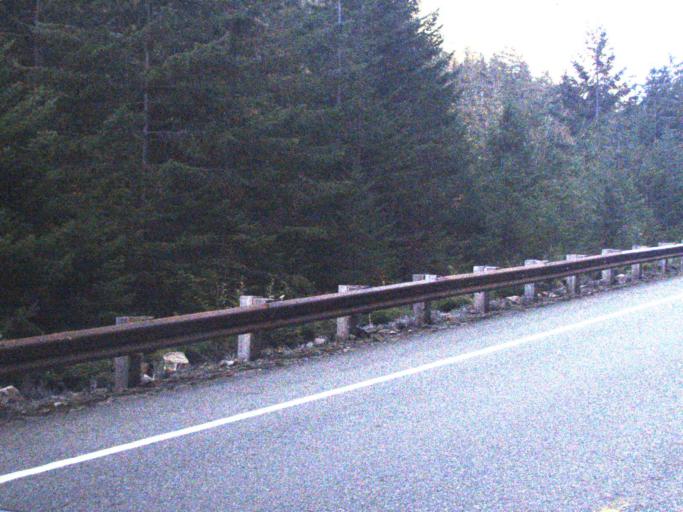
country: US
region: Washington
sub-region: Snohomish County
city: Darrington
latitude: 48.6757
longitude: -120.8801
